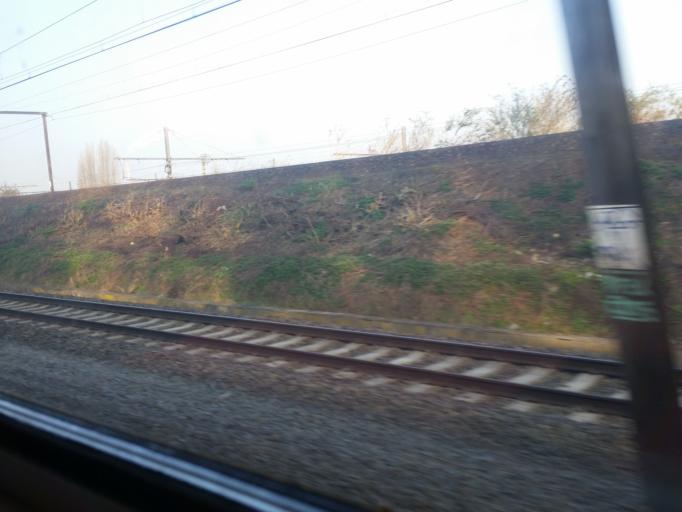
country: BE
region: Flanders
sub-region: Provincie Vlaams-Brabant
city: Diegem
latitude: 50.8839
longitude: 4.4031
